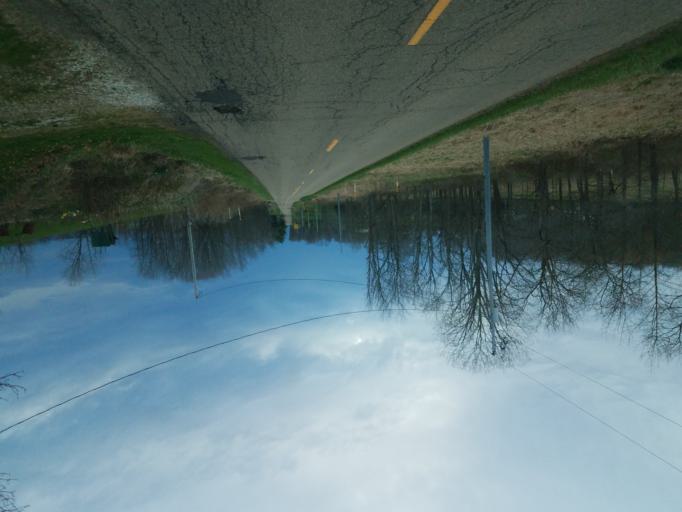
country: US
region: Ohio
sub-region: Knox County
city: Mount Vernon
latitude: 40.4944
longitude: -82.4201
